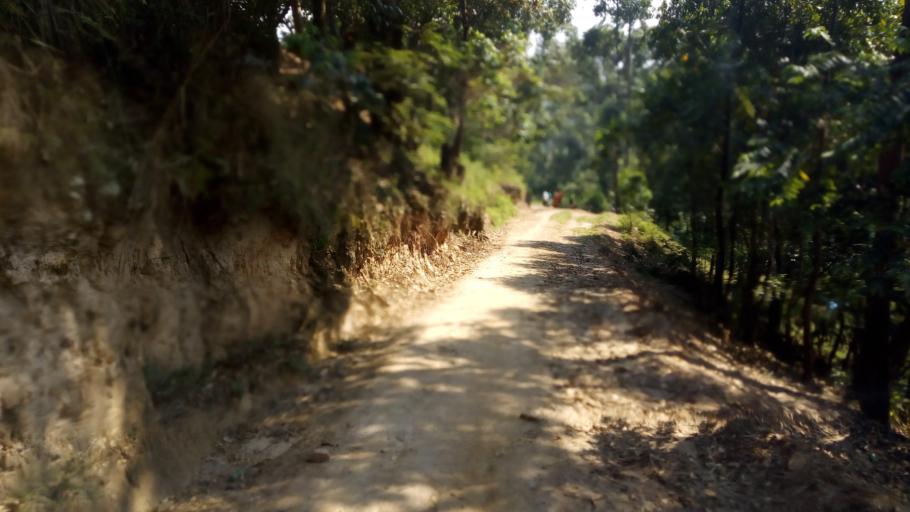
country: UG
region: Western Region
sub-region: Kisoro District
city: Kisoro
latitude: -1.0937
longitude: 29.5859
